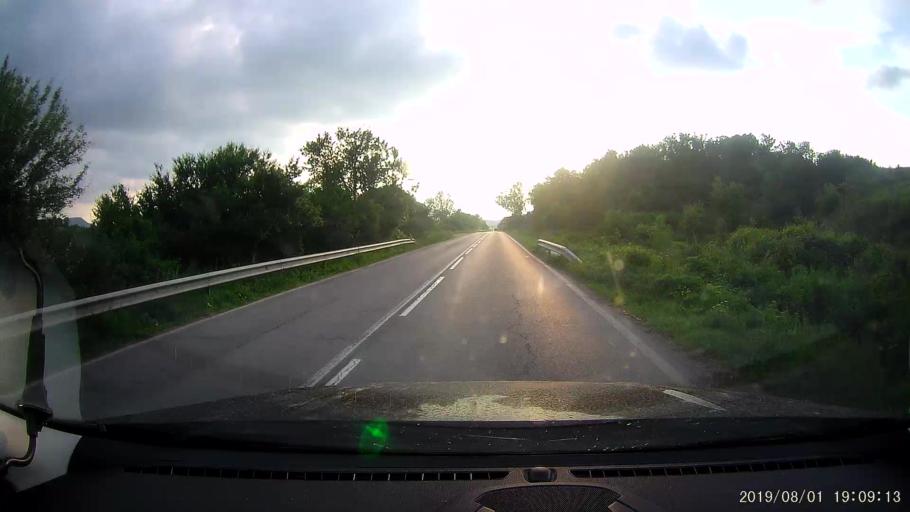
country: BG
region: Shumen
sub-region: Obshtina Smyadovo
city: Smyadovo
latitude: 42.9835
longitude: 27.0091
